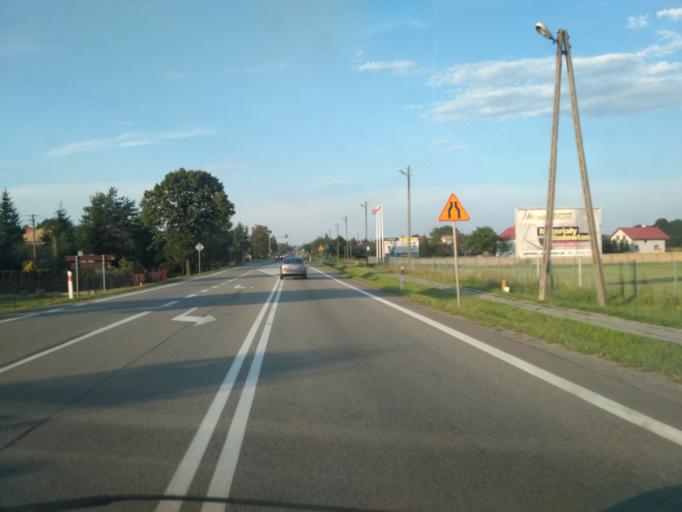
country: PL
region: Subcarpathian Voivodeship
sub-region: Powiat krosnienski
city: Miejsce Piastowe
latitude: 49.6146
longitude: 21.7506
